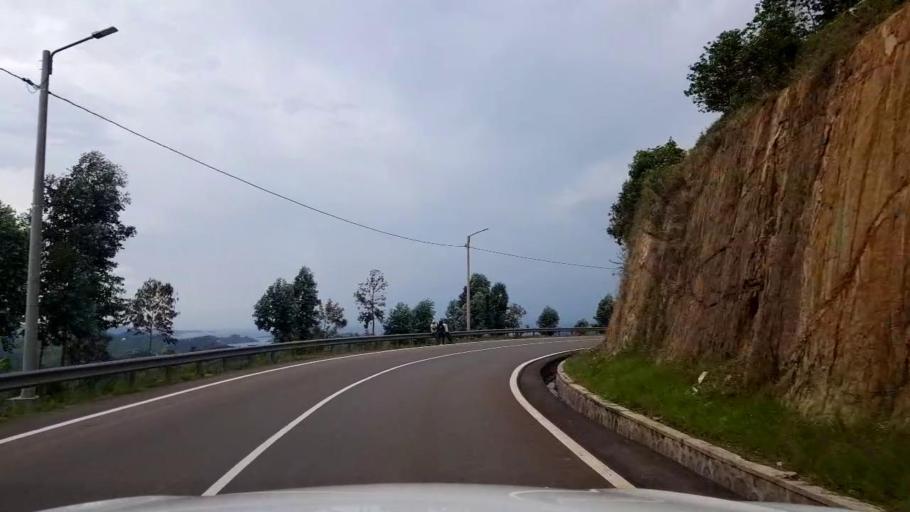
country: RW
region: Western Province
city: Kibuye
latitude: -2.0248
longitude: 29.3893
